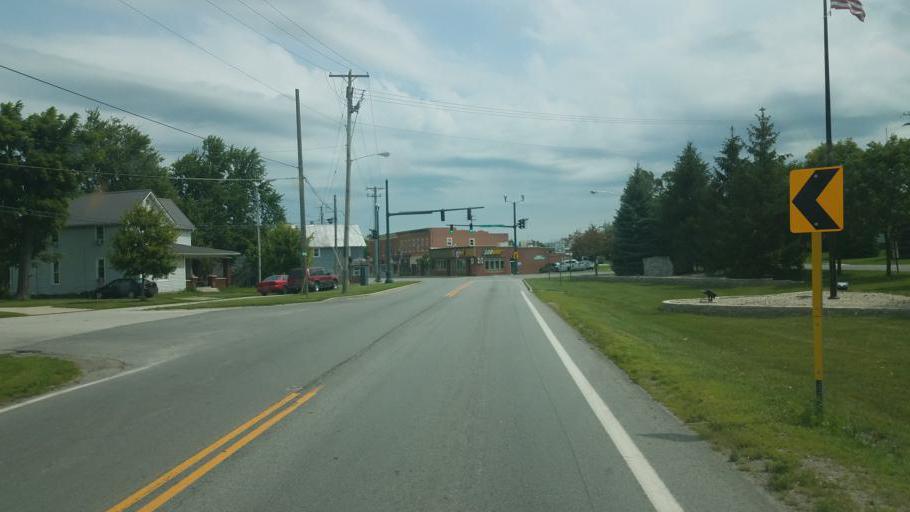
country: US
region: Ohio
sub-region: Wyandot County
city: Carey
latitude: 40.9499
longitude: -83.3840
